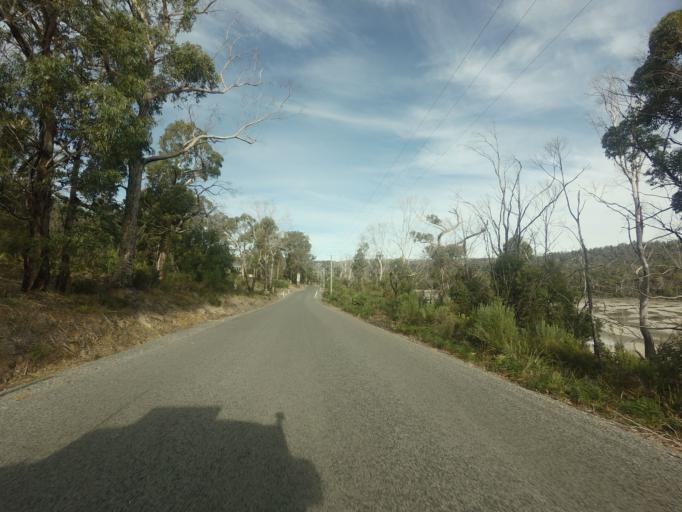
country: AU
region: Tasmania
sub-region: Sorell
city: Sorell
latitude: -42.9551
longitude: 147.8520
